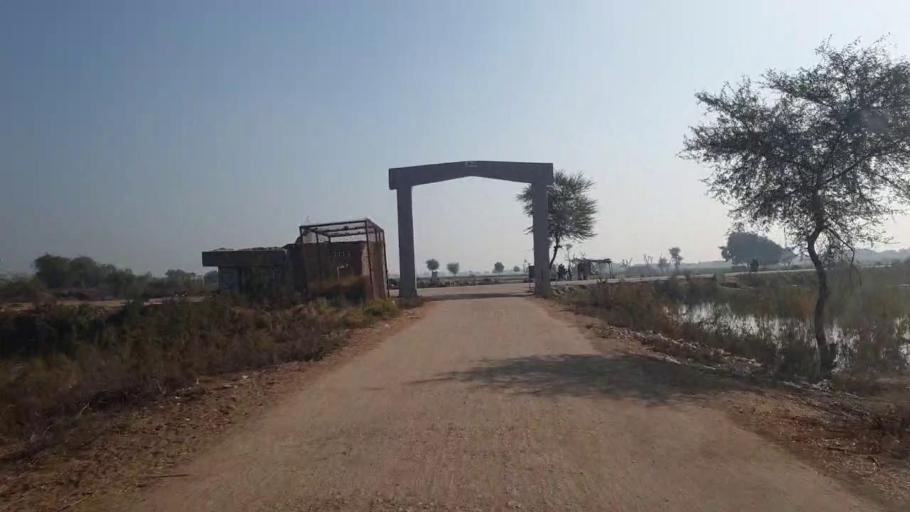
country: PK
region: Sindh
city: Shahdadpur
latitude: 25.9472
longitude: 68.5958
